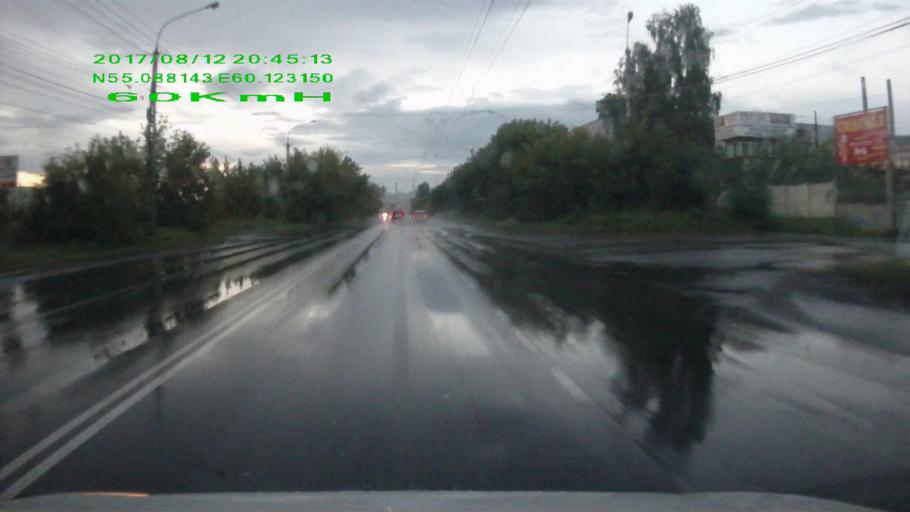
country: RU
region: Chelyabinsk
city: Miass
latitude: 55.0882
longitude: 60.1232
